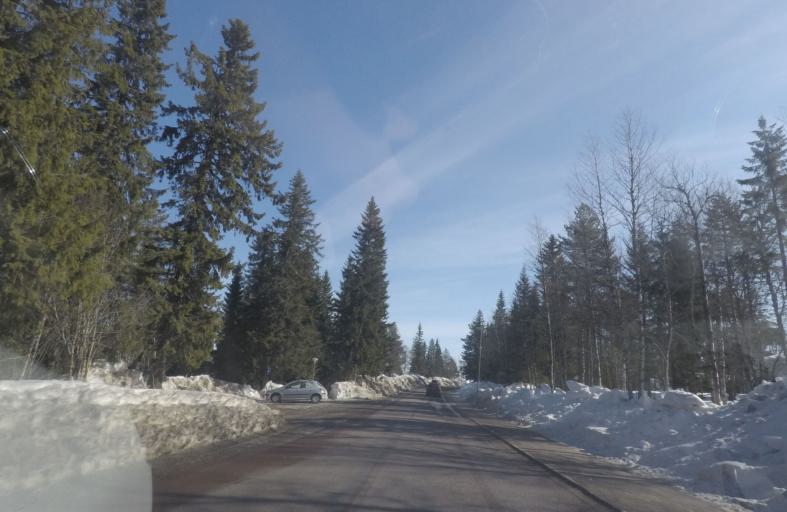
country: SE
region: Dalarna
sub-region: Malung-Saelens kommun
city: Malung
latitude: 61.1677
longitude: 13.1670
